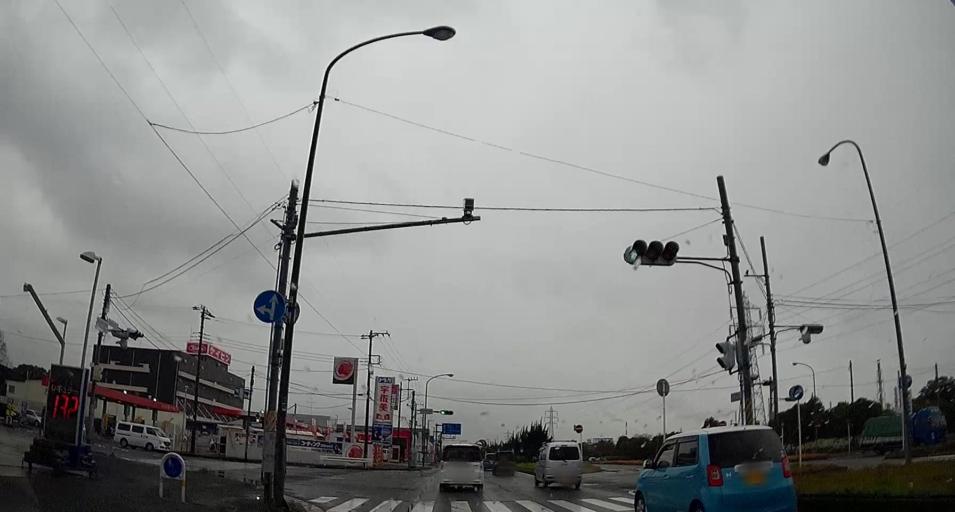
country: JP
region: Chiba
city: Ichihara
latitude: 35.5196
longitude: 140.0616
